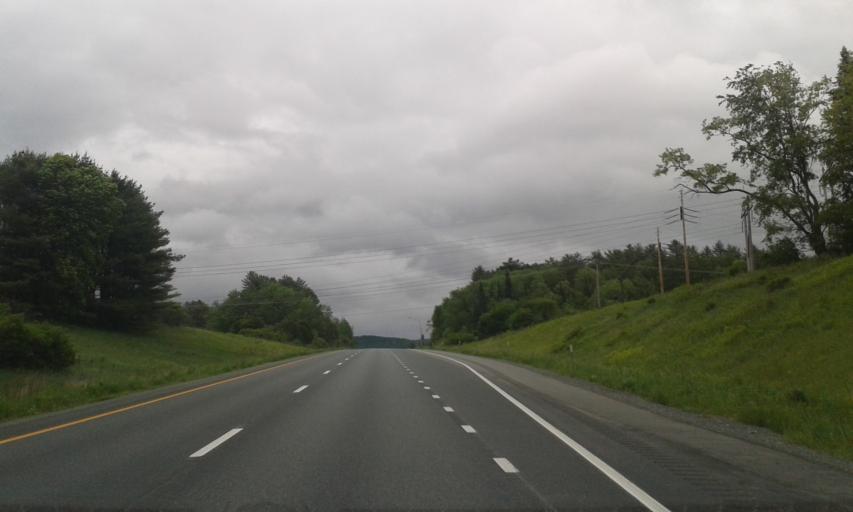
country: US
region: New Hampshire
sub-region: Grafton County
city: Littleton
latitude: 44.3333
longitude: -71.8840
